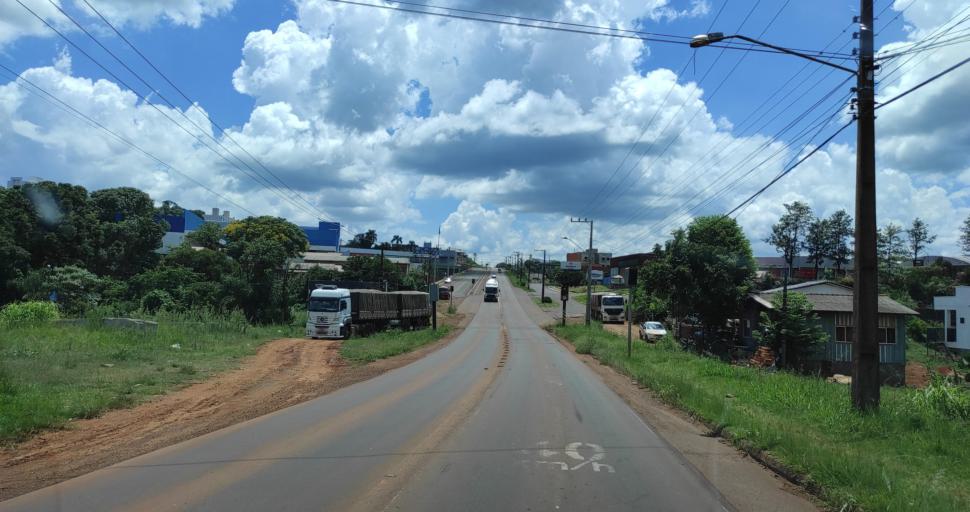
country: BR
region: Santa Catarina
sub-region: Xanxere
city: Xanxere
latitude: -26.8615
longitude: -52.4065
